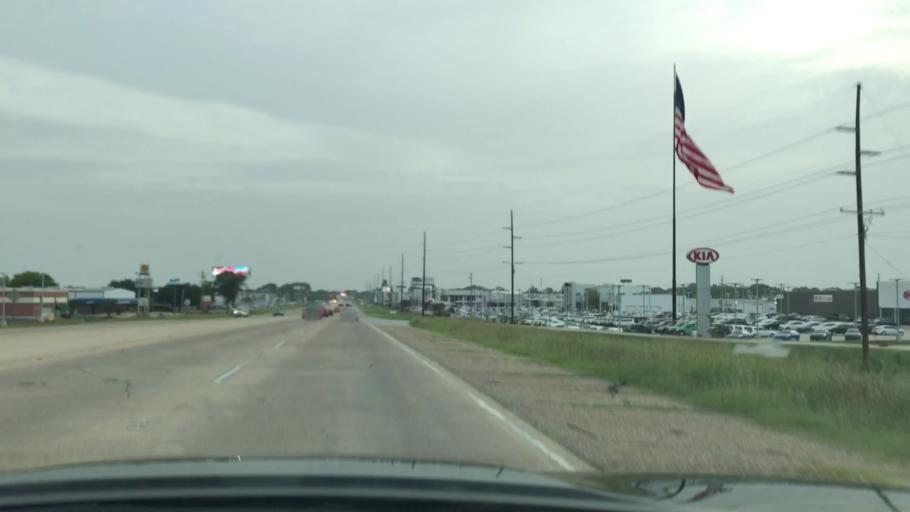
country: US
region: Louisiana
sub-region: Bossier Parish
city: Bossier City
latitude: 32.4155
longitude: -93.7232
